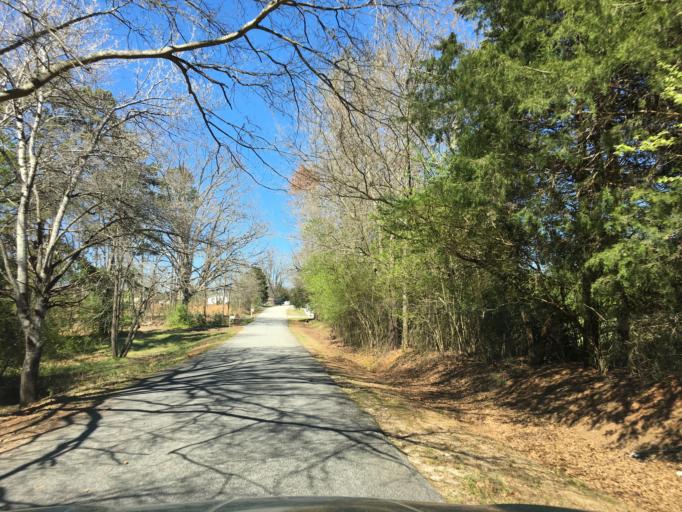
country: US
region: South Carolina
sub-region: Spartanburg County
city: Woodruff
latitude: 34.7988
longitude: -82.0858
